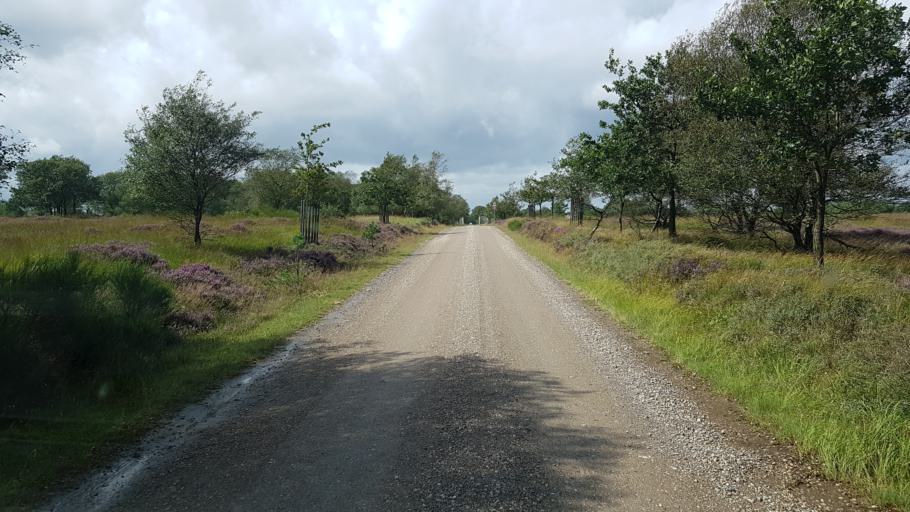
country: DK
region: South Denmark
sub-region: Vejen Kommune
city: Holsted
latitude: 55.5958
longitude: 8.8787
